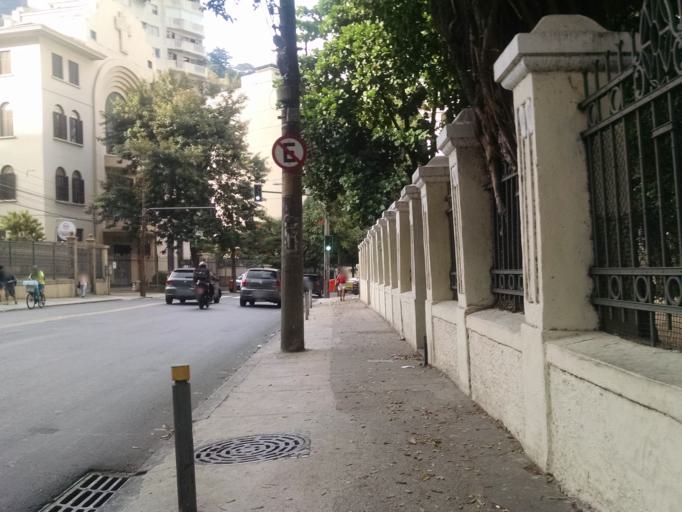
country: BR
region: Rio de Janeiro
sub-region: Rio De Janeiro
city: Rio de Janeiro
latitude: -22.9392
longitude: -43.1960
